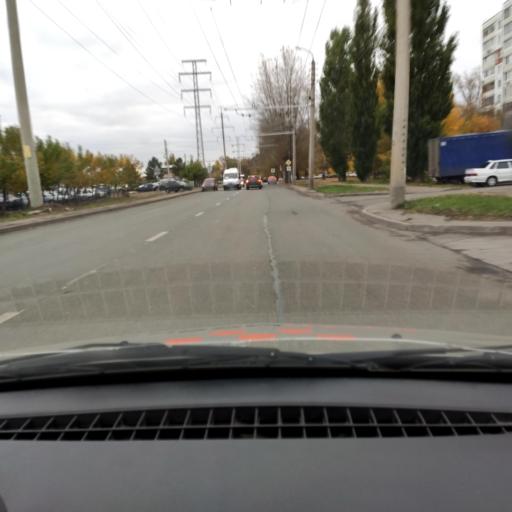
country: RU
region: Bashkortostan
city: Ufa
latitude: 54.7939
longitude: 56.0562
